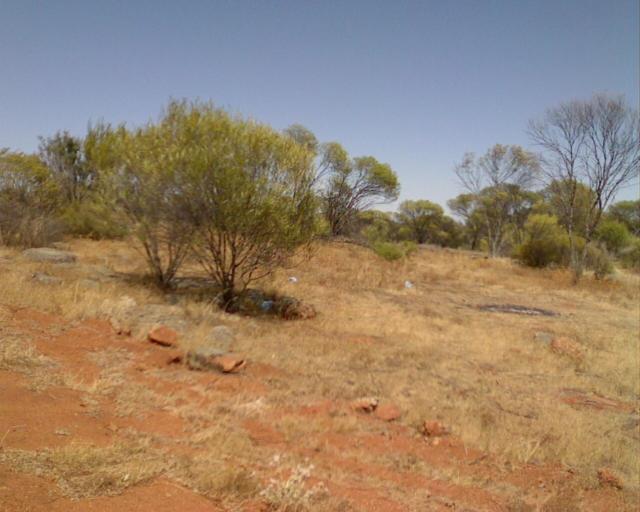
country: AU
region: Western Australia
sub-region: Wongan-Ballidu
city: Wongan Hills
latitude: -30.4236
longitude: 116.9676
